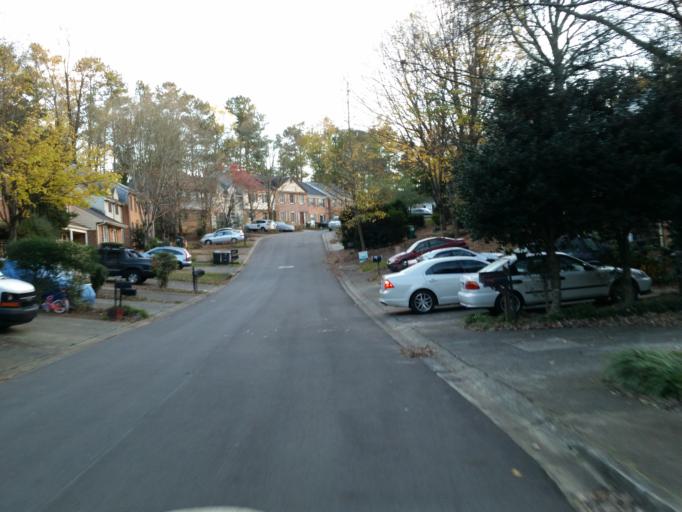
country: US
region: Georgia
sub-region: Cobb County
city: Smyrna
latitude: 33.9175
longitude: -84.4732
